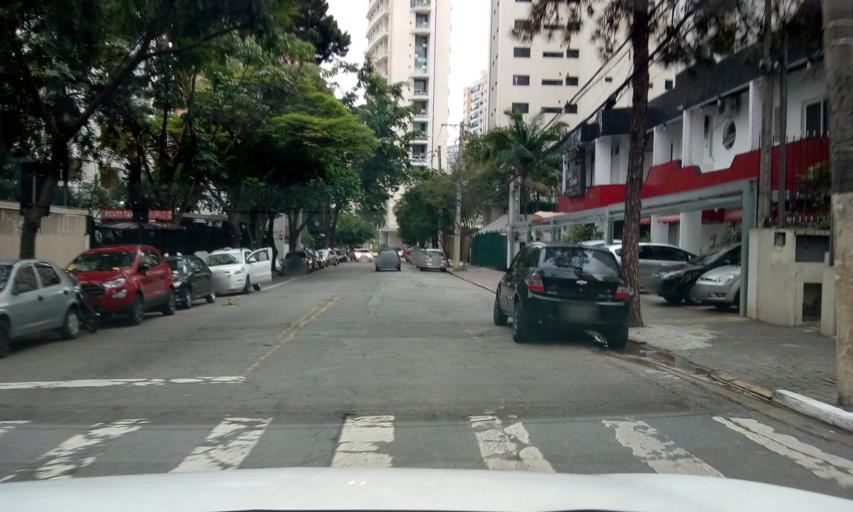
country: BR
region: Sao Paulo
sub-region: Sao Paulo
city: Sao Paulo
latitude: -23.6010
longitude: -46.6681
